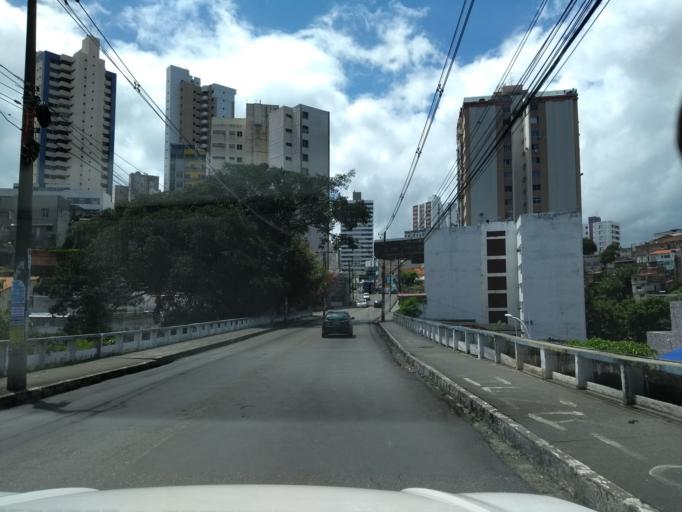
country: BR
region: Bahia
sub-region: Salvador
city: Salvador
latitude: -12.9967
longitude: -38.5161
